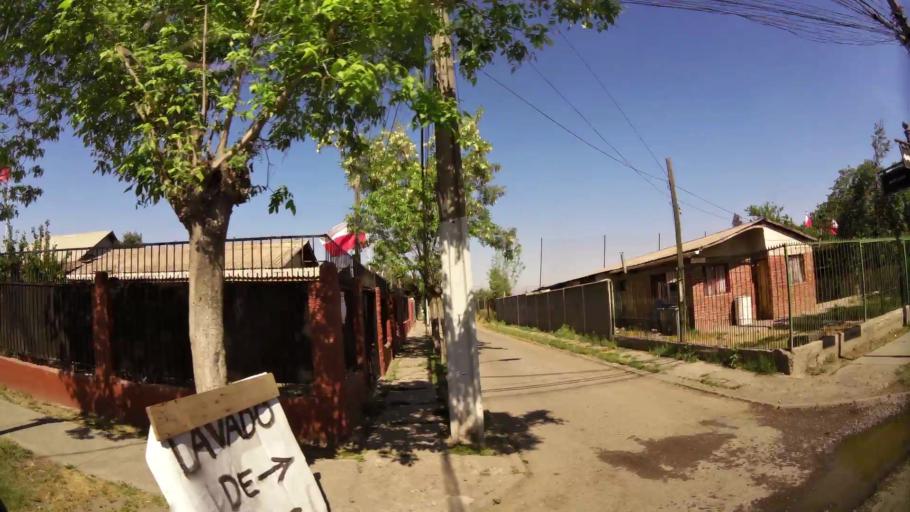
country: CL
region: Santiago Metropolitan
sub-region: Provincia de Talagante
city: Penaflor
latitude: -33.5675
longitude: -70.8015
